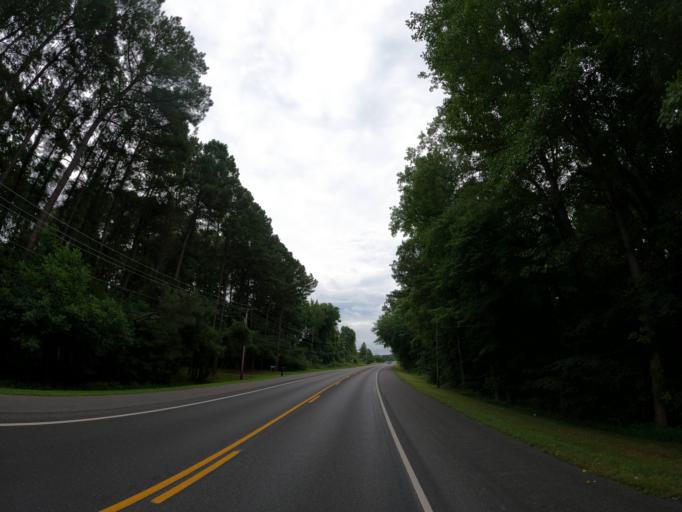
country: US
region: Maryland
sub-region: Saint Mary's County
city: California
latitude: 38.2306
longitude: -76.5192
